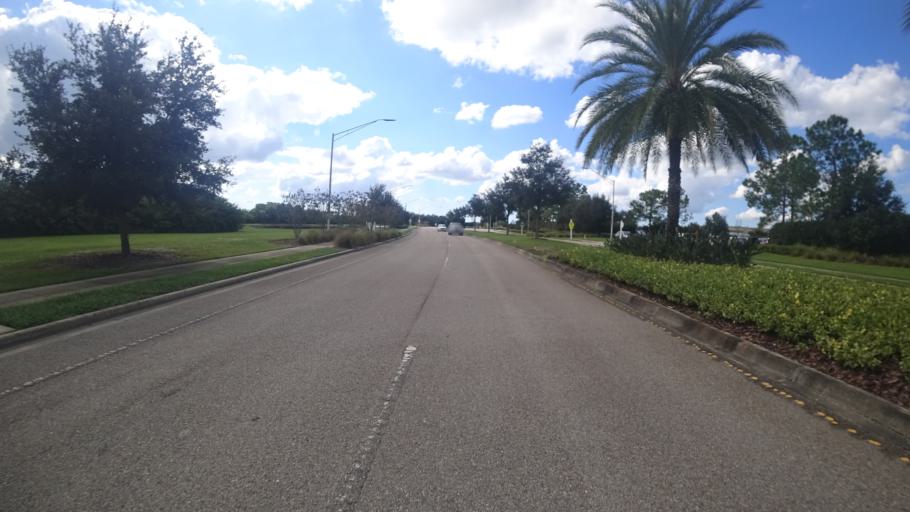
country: US
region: Florida
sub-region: Sarasota County
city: The Meadows
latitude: 27.3976
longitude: -82.3902
